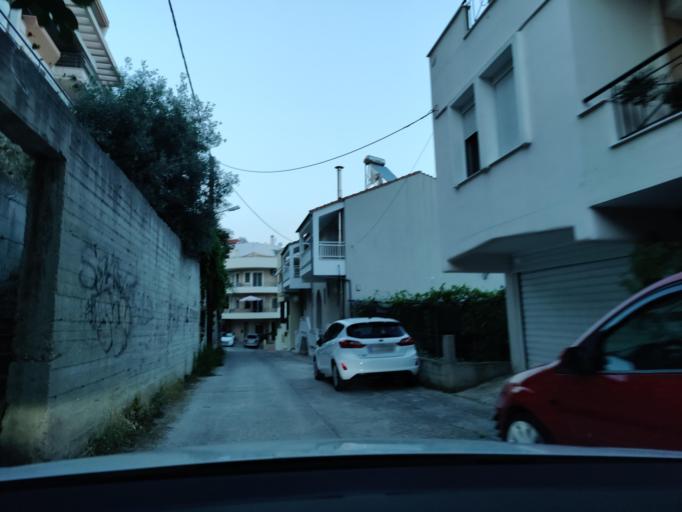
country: GR
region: East Macedonia and Thrace
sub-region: Nomos Kavalas
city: Kavala
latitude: 40.9259
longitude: 24.3806
